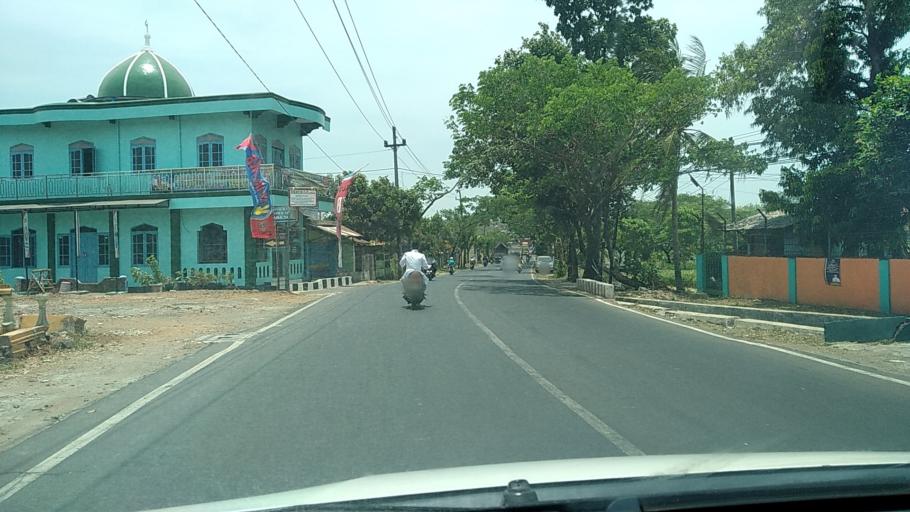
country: ID
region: Central Java
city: Ungaran
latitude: -7.0824
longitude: 110.3094
